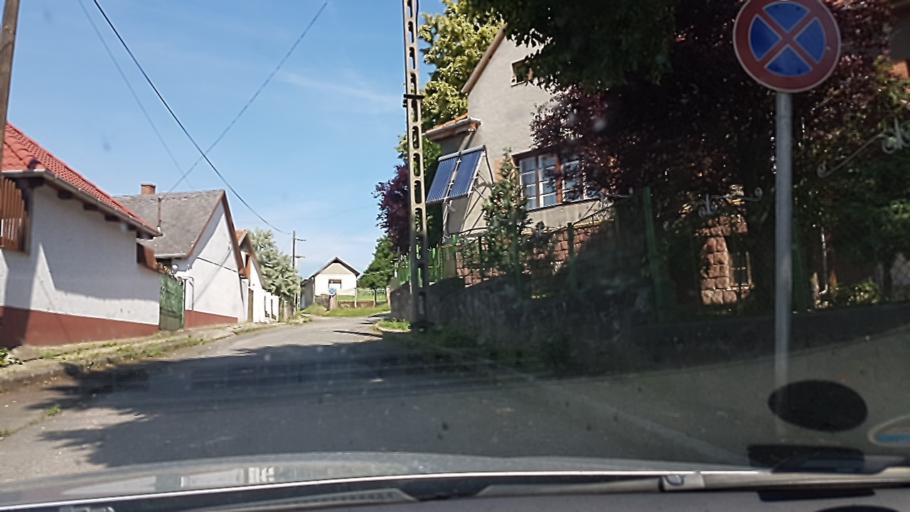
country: HU
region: Borsod-Abauj-Zemplen
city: Saly
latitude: 47.9583
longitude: 20.6925
